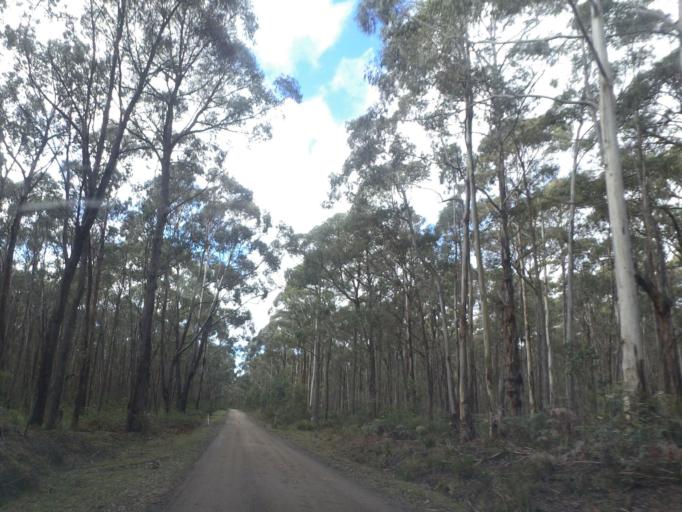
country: AU
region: Victoria
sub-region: Moorabool
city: Bacchus Marsh
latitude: -37.4327
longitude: 144.4560
